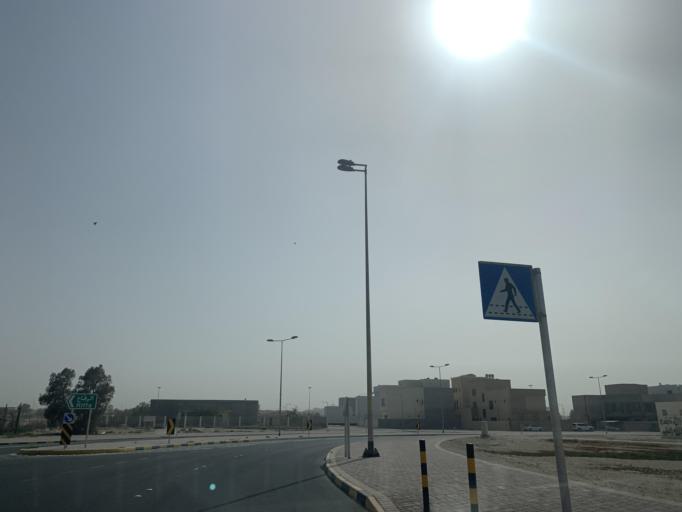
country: BH
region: Northern
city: Madinat `Isa
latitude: 26.1620
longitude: 50.5385
